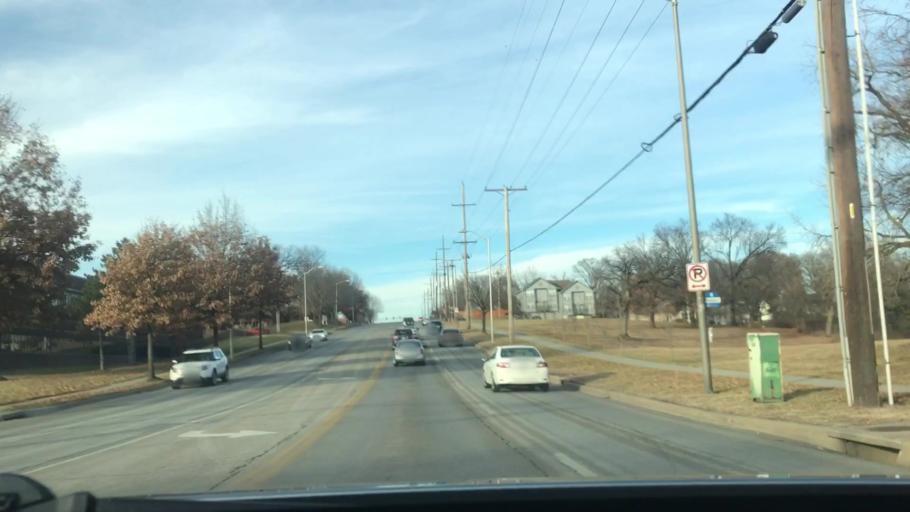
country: US
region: Missouri
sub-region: Clay County
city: Gladstone
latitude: 39.1918
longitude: -94.5765
